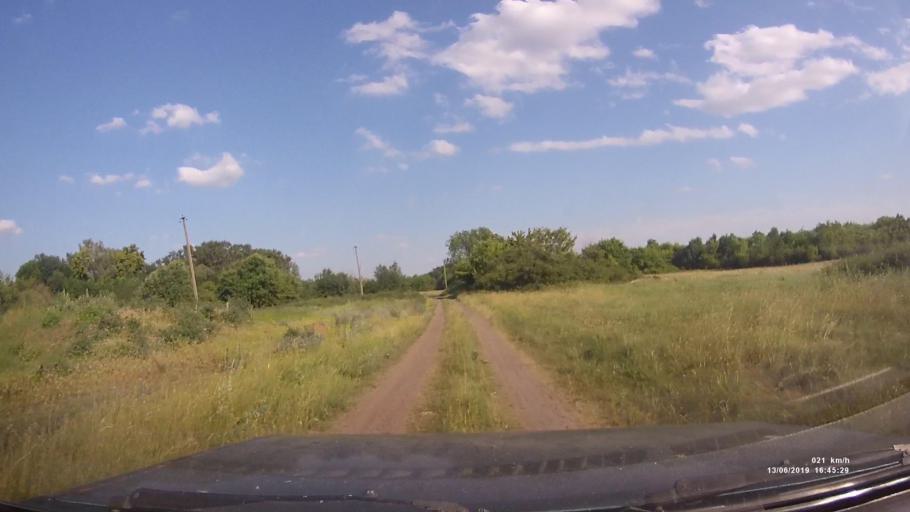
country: RU
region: Rostov
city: Kazanskaya
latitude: 49.9478
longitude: 41.4230
